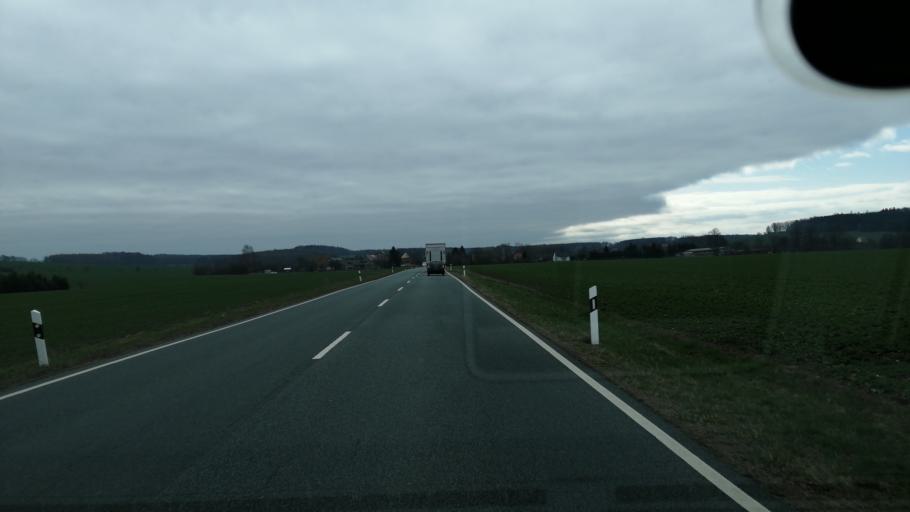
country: DE
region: Saxony
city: Niedercunnersdorf
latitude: 51.0688
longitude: 14.6857
